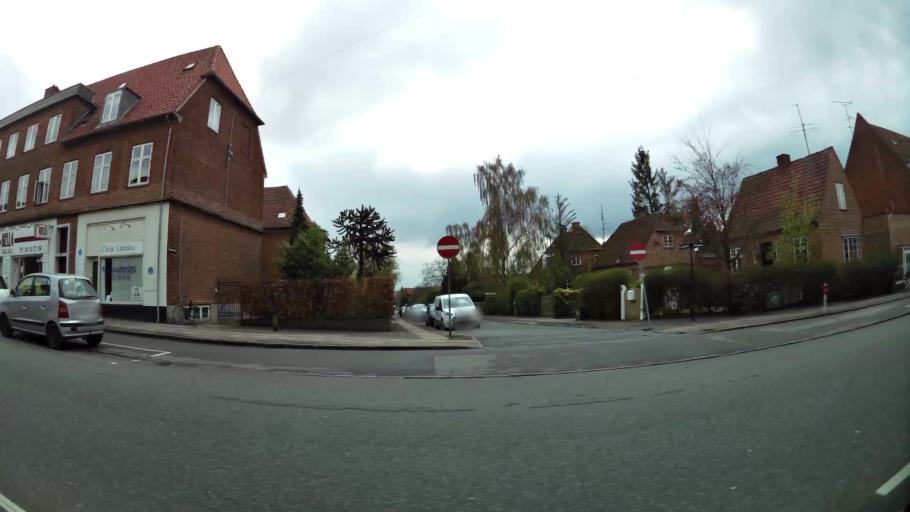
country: DK
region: Capital Region
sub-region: Kobenhavn
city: Vanlose
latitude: 55.6959
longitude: 12.5022
